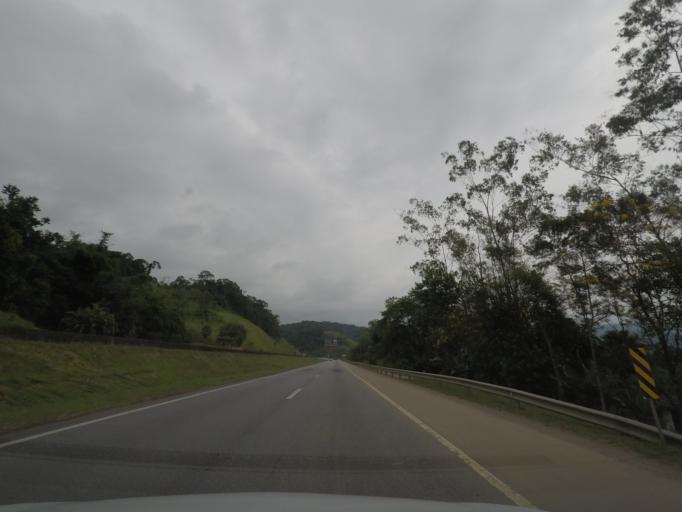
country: BR
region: Sao Paulo
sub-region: Miracatu
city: Miracatu
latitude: -24.1821
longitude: -47.3544
